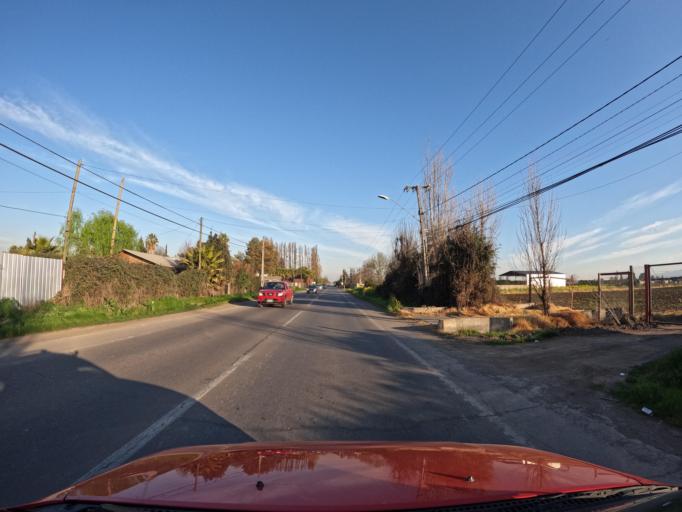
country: CL
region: Maule
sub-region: Provincia de Curico
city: Curico
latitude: -34.9508
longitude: -71.2569
